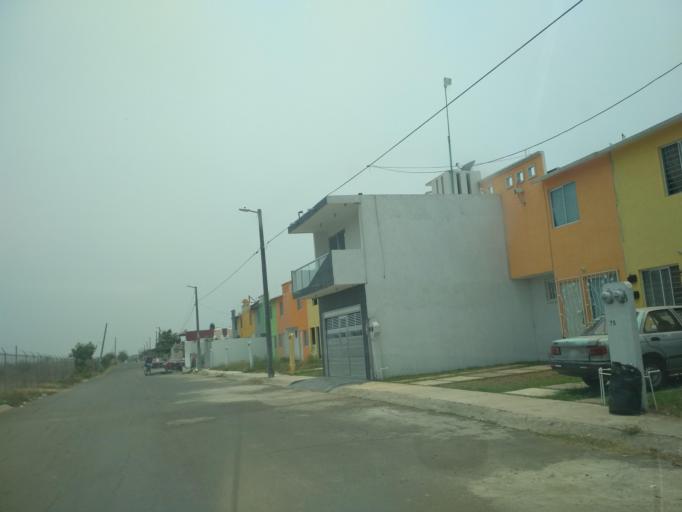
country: MX
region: Veracruz
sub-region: Veracruz
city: Las Amapolas
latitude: 19.1534
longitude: -96.2143
